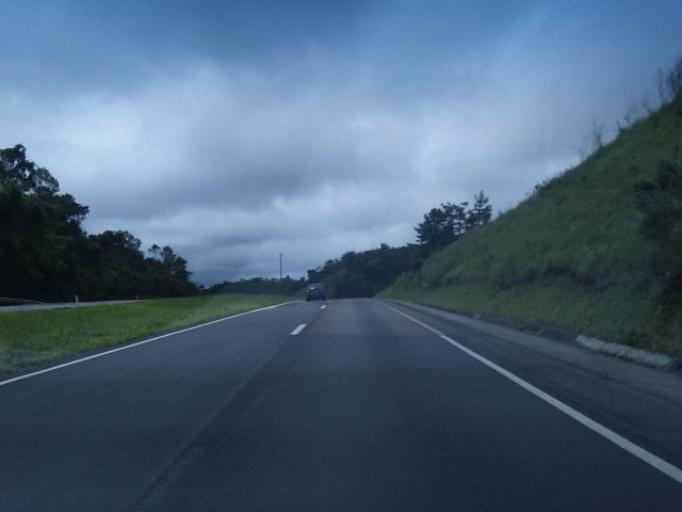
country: BR
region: Parana
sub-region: Antonina
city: Antonina
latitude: -25.0911
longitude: -48.6473
